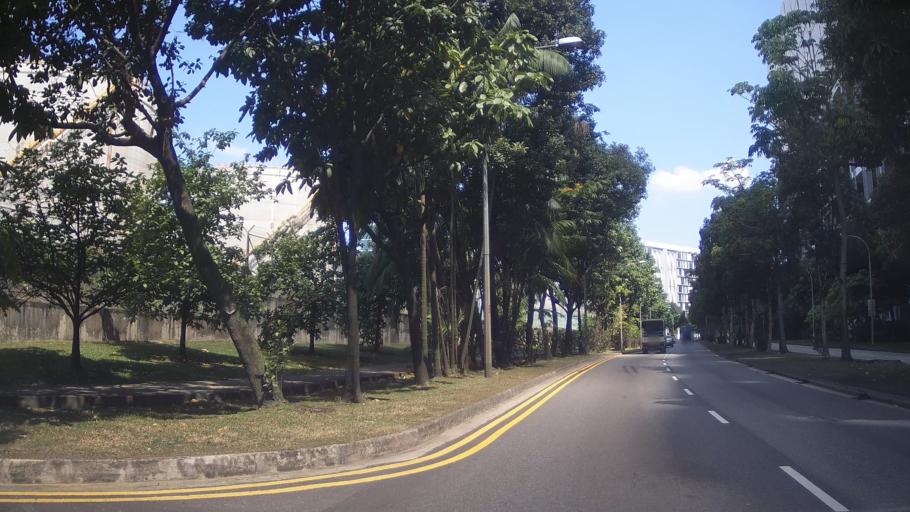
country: SG
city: Singapore
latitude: 1.3105
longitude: 103.6971
